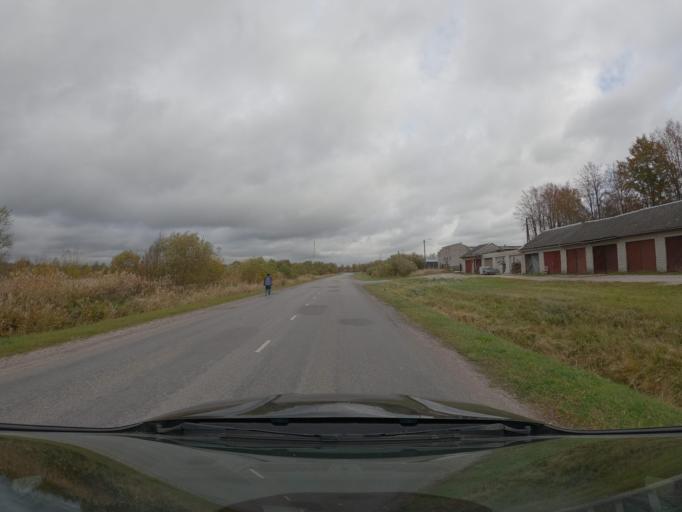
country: EE
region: Saare
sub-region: Kuressaare linn
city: Kuressaare
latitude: 58.2658
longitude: 22.4836
